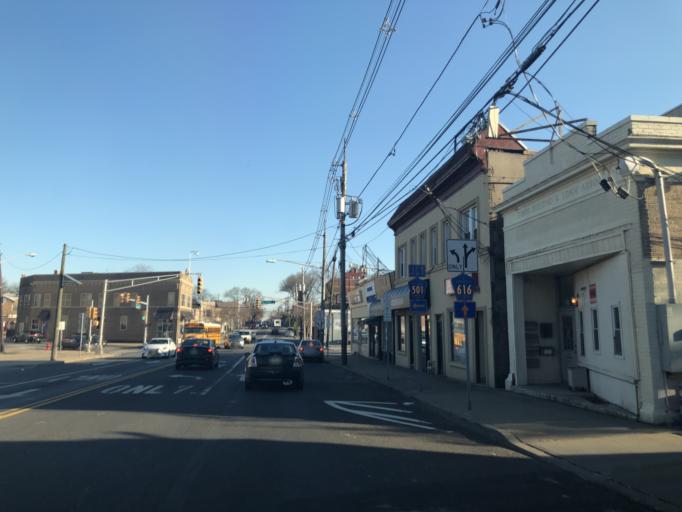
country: US
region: New Jersey
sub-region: Middlesex County
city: Fords
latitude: 40.5291
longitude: -74.3168
